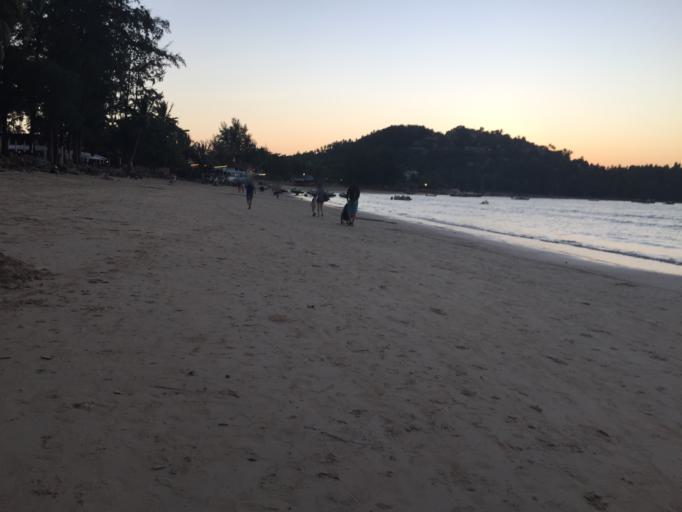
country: TH
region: Phuket
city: Thalang
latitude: 7.9866
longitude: 98.2872
